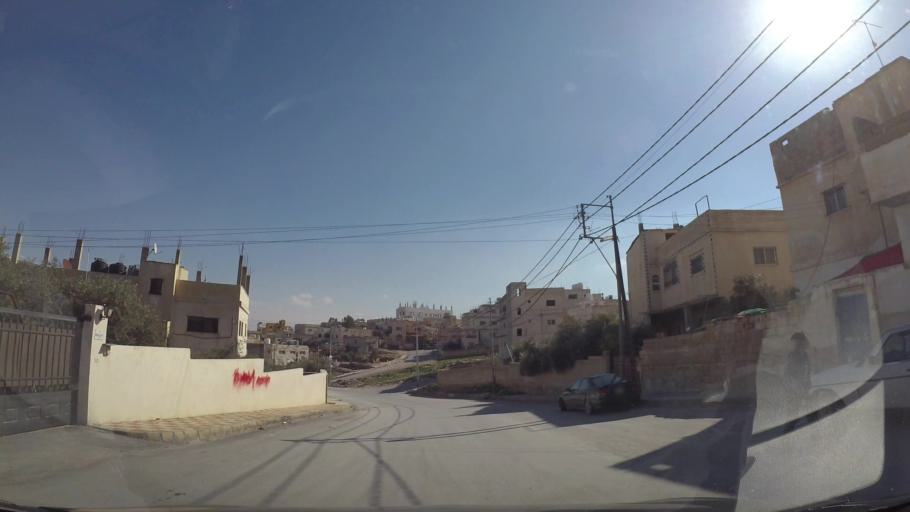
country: JO
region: Zarqa
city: Russeifa
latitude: 32.0373
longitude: 36.0327
